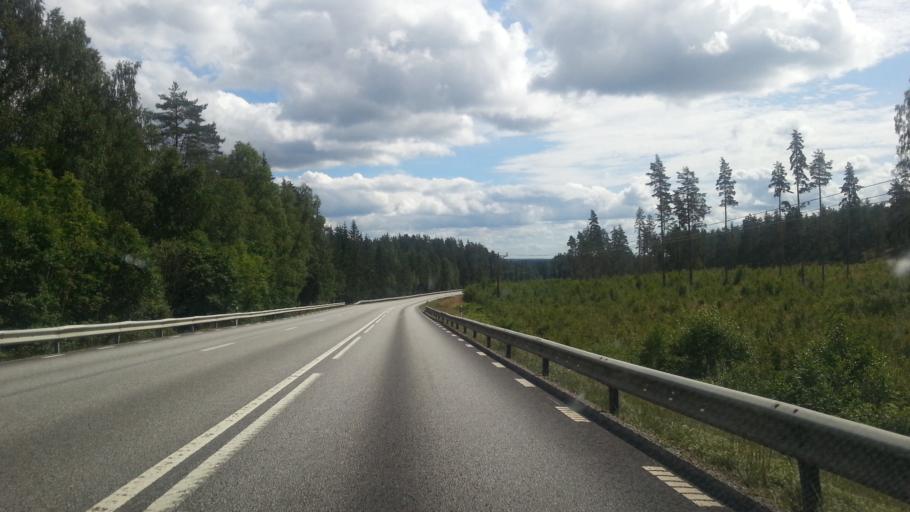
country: SE
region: OErebro
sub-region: Lindesbergs Kommun
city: Stora
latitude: 59.6421
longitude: 15.1434
